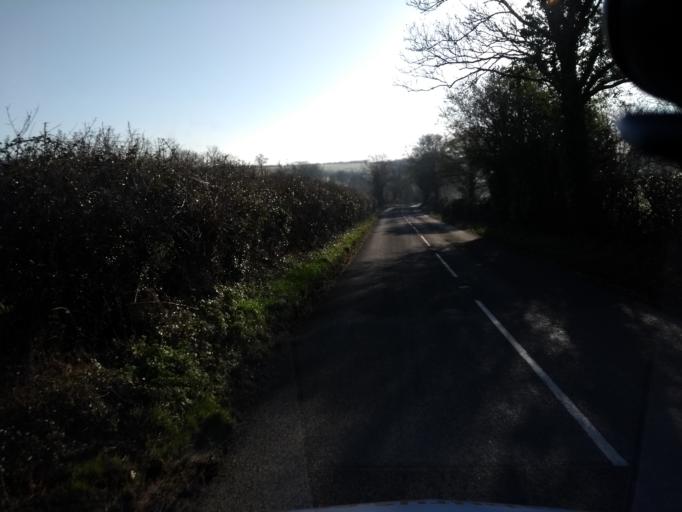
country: GB
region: England
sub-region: Somerset
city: Redlynch
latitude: 51.0915
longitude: -2.4178
